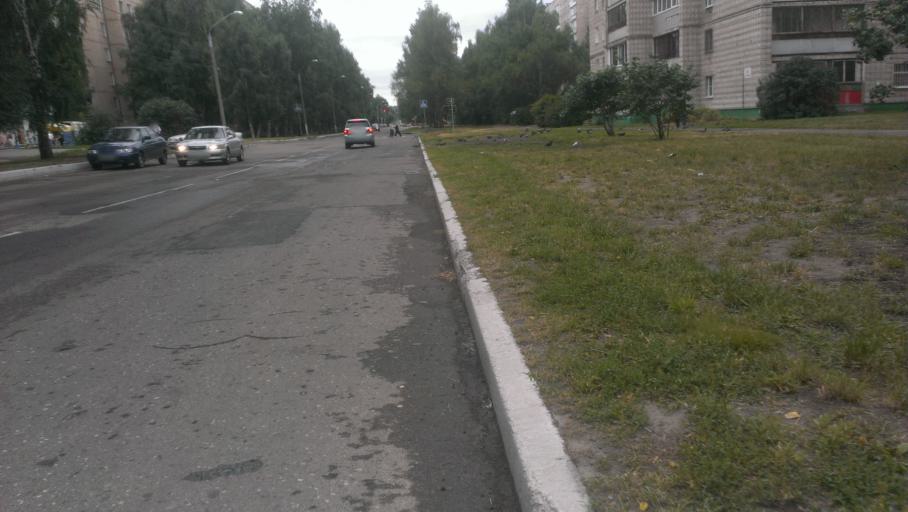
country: RU
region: Altai Krai
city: Novosilikatnyy
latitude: 53.3701
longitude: 83.6692
